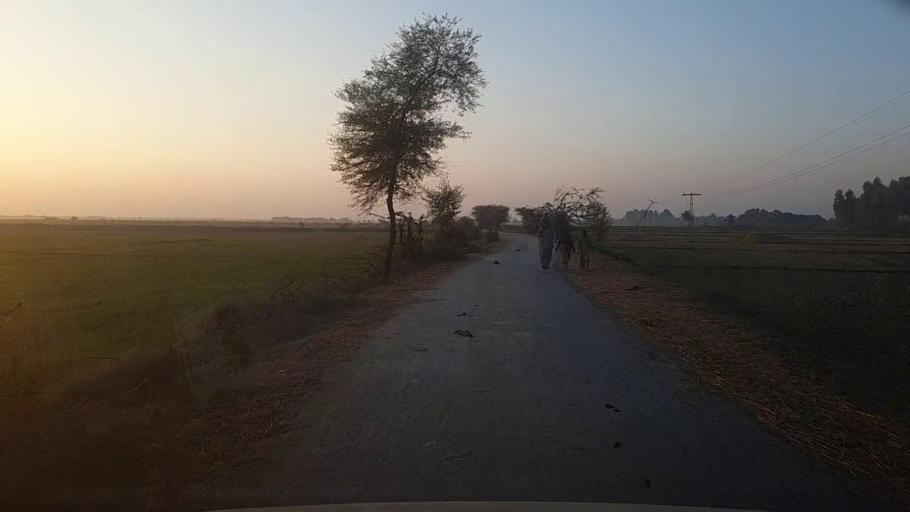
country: PK
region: Sindh
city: Khairpur Nathan Shah
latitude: 27.1533
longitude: 67.7310
